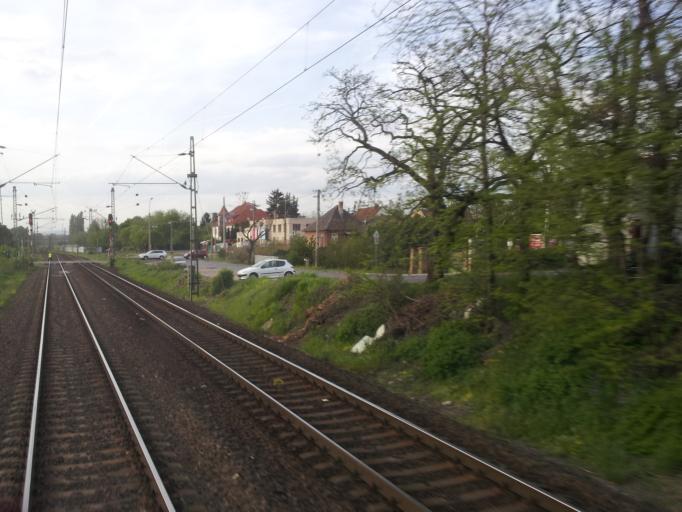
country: HU
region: Budapest
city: Budapest XVI. keruelet
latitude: 47.5133
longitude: 19.1528
